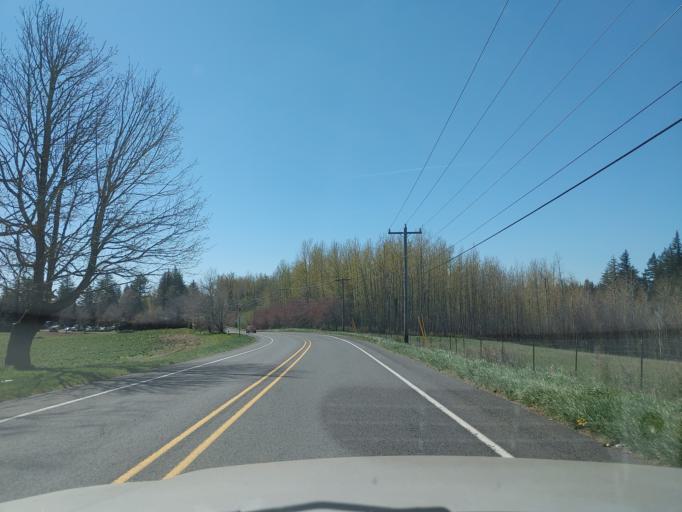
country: US
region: Washington
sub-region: Clark County
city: Washougal
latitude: 45.5294
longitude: -122.3005
